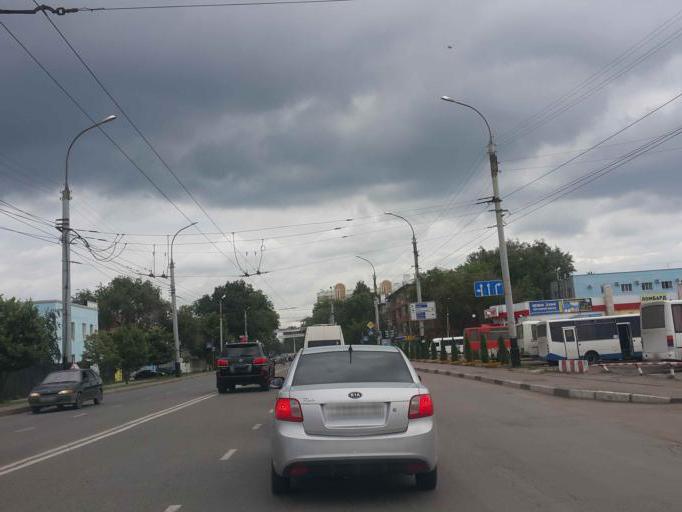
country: RU
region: Tambov
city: Tambov
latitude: 52.7376
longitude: 41.4384
